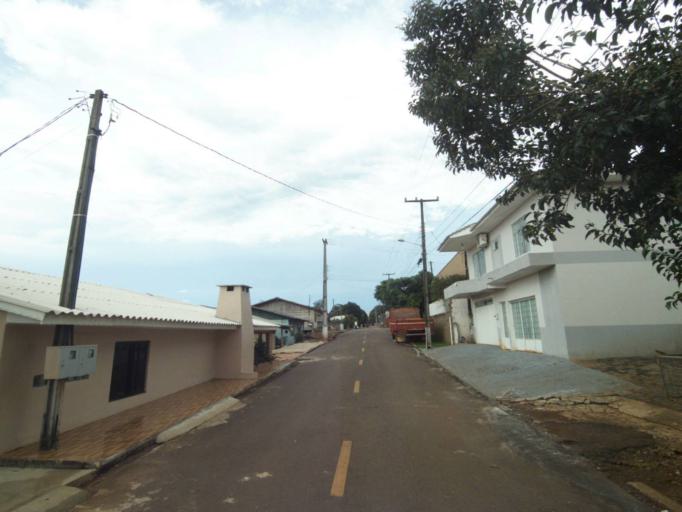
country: BR
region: Parana
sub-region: Guaraniacu
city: Guaraniacu
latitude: -25.1021
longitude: -52.8715
